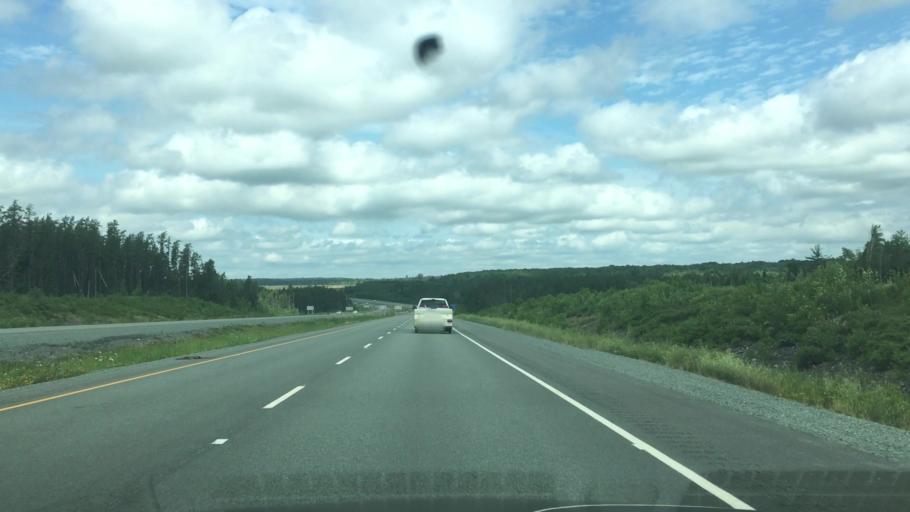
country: CA
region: Nova Scotia
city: Oxford
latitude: 45.6794
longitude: -63.7621
